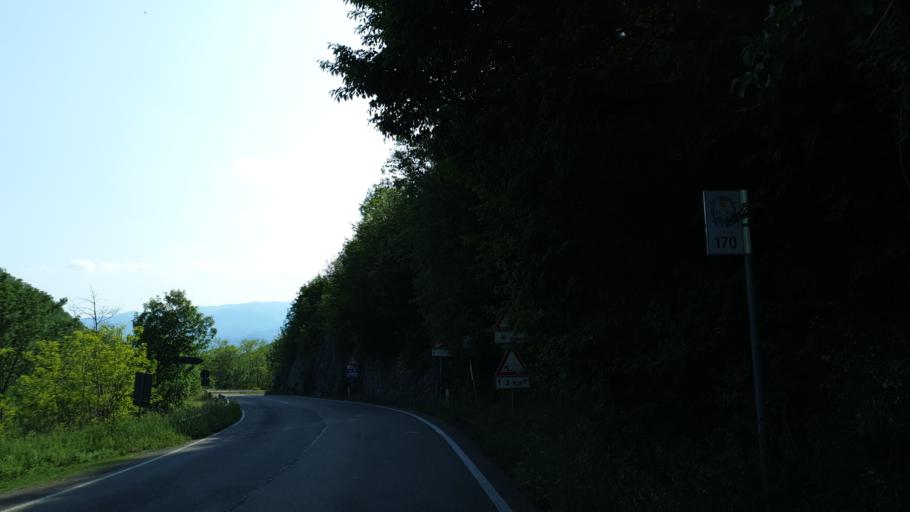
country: IT
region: Tuscany
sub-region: Province of Arezzo
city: Soci
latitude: 43.7703
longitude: 11.8447
